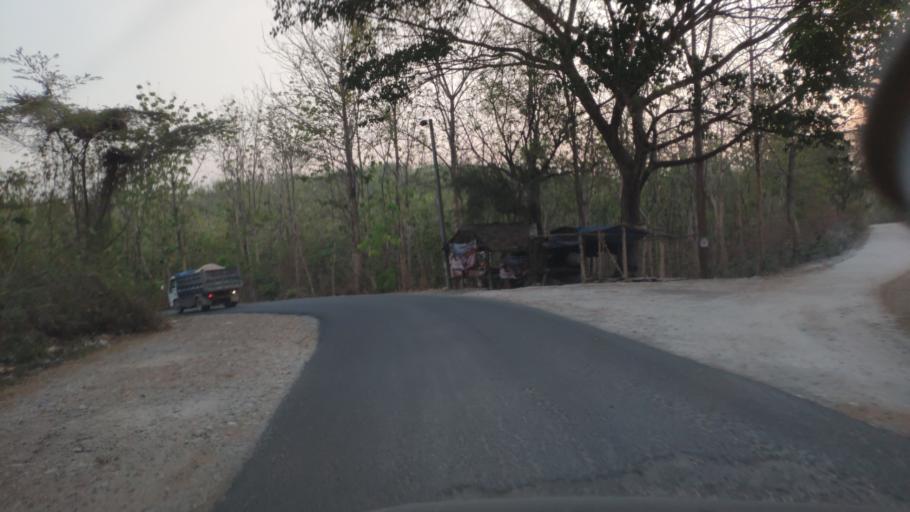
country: ID
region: Central Java
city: Semanggi
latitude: -7.0707
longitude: 111.4129
